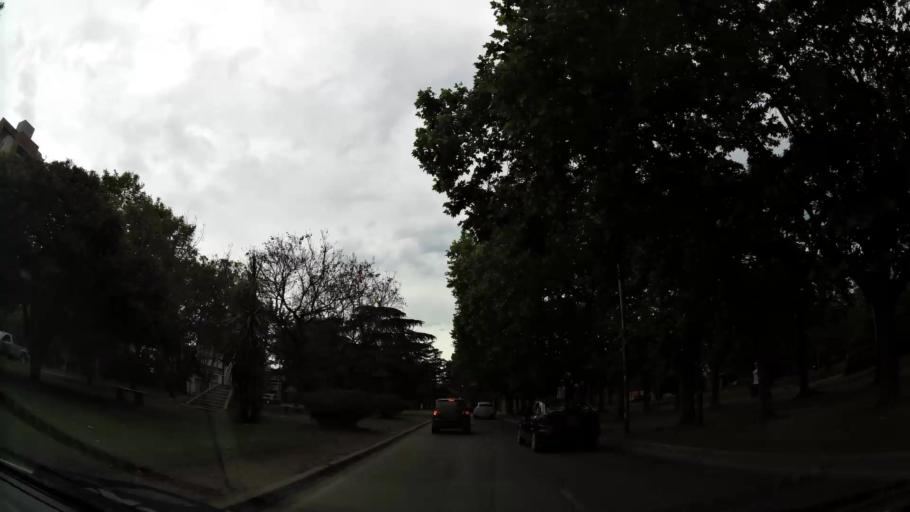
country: AR
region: Buenos Aires
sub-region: Partido de Quilmes
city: Quilmes
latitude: -34.8042
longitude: -58.2785
